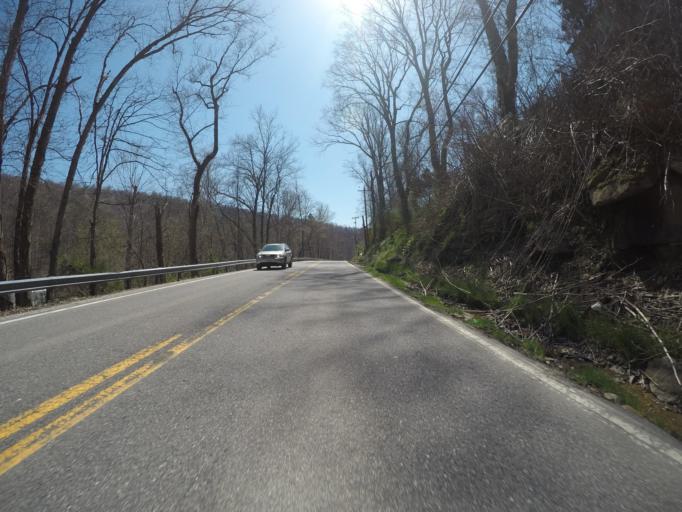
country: US
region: West Virginia
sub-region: Kanawha County
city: Coal Fork
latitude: 38.3833
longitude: -81.5608
